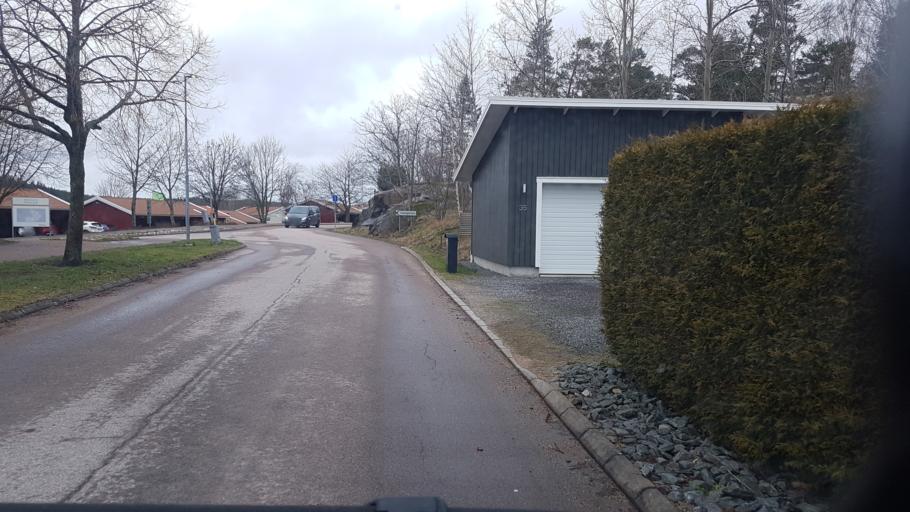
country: SE
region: Vaestra Goetaland
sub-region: Lerums Kommun
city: Stenkullen
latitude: 57.7878
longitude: 12.3027
